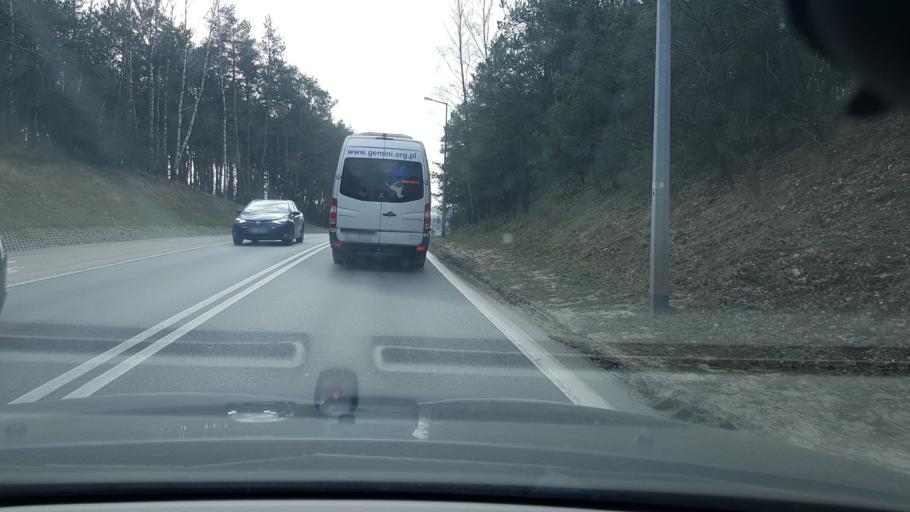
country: PL
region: Masovian Voivodeship
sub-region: Warszawa
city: Wesola
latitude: 52.2270
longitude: 21.2238
